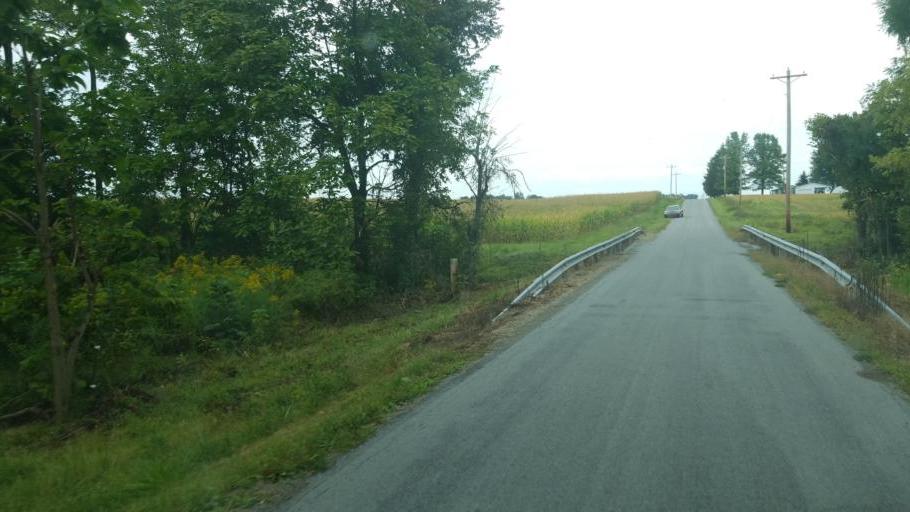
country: US
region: Ohio
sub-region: Wyandot County
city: Upper Sandusky
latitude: 40.8969
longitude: -83.1893
